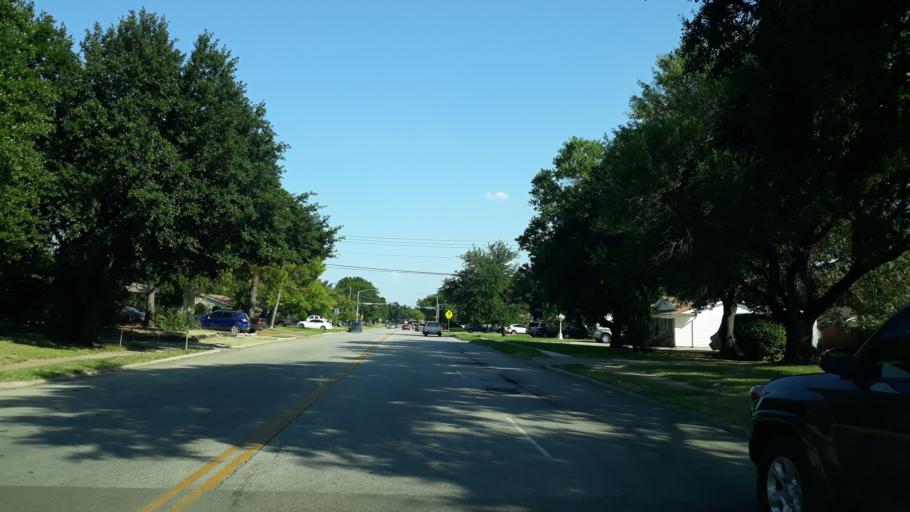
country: US
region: Texas
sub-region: Dallas County
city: Irving
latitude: 32.8446
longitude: -96.9835
